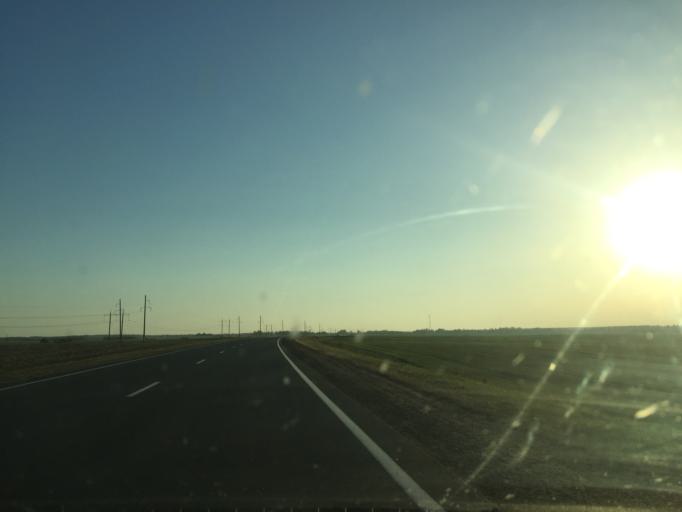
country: BY
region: Mogilev
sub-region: Mahilyowski Rayon
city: Kadino
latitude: 53.8302
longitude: 30.4770
